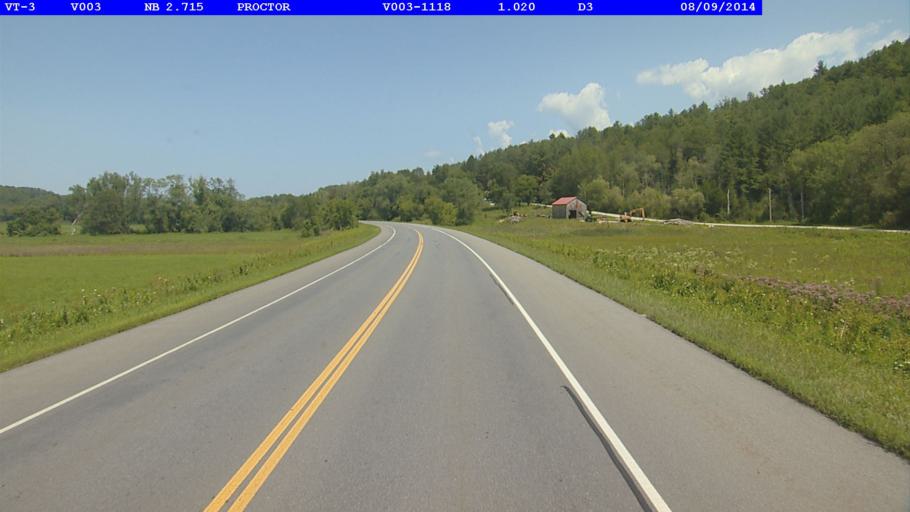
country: US
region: Vermont
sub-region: Rutland County
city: West Rutland
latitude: 43.6386
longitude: -73.0330
